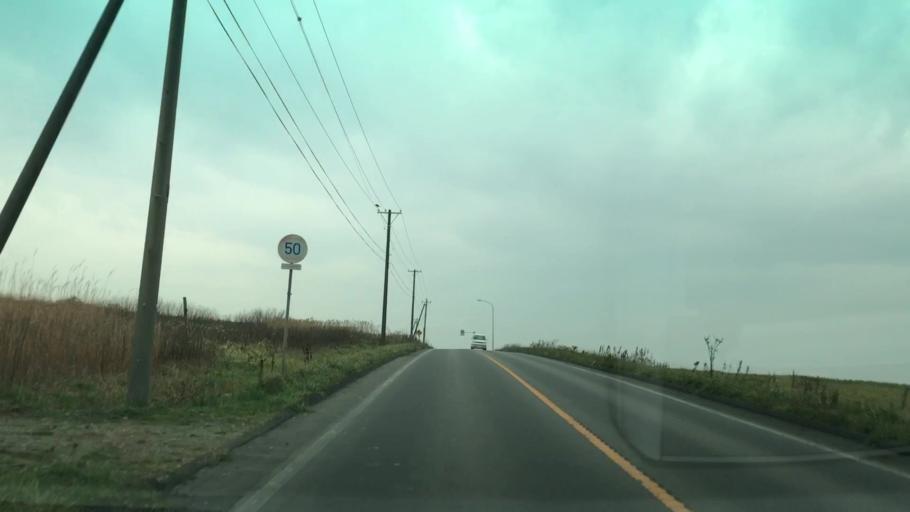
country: JP
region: Hokkaido
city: Ishikari
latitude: 43.3513
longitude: 141.4263
